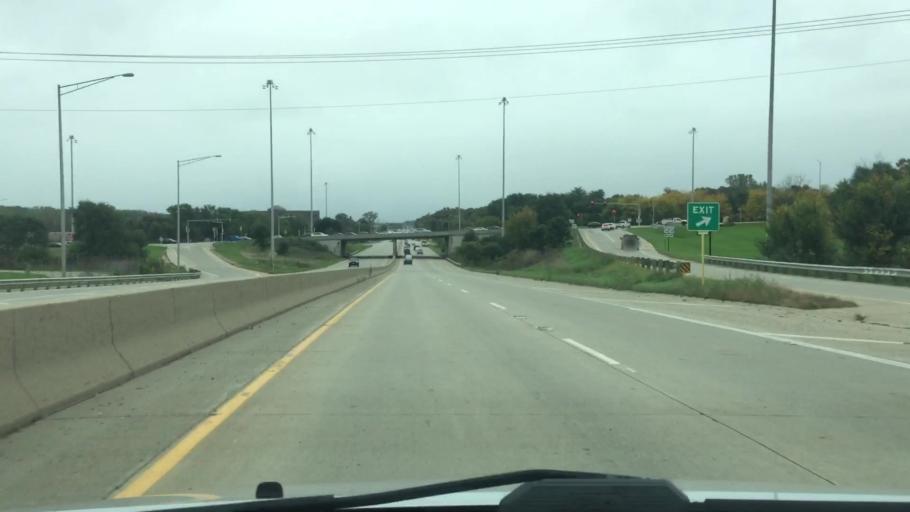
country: US
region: Illinois
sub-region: McHenry County
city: Crystal Lake
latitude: 42.2279
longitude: -88.2877
